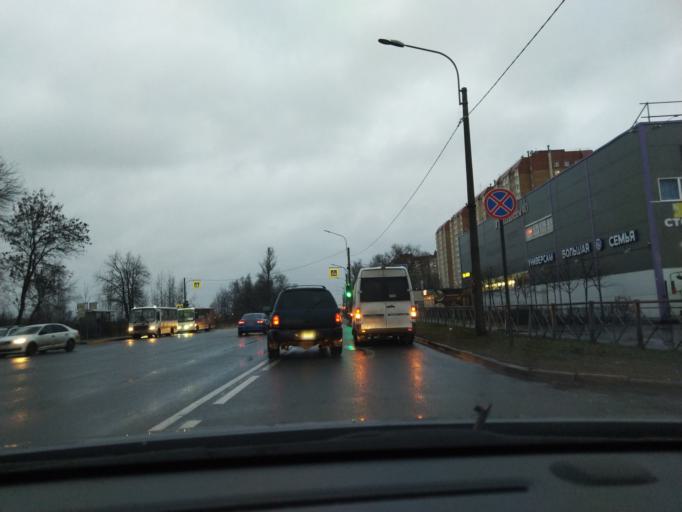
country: RU
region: St.-Petersburg
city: Gorelovo
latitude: 59.7882
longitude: 30.1431
